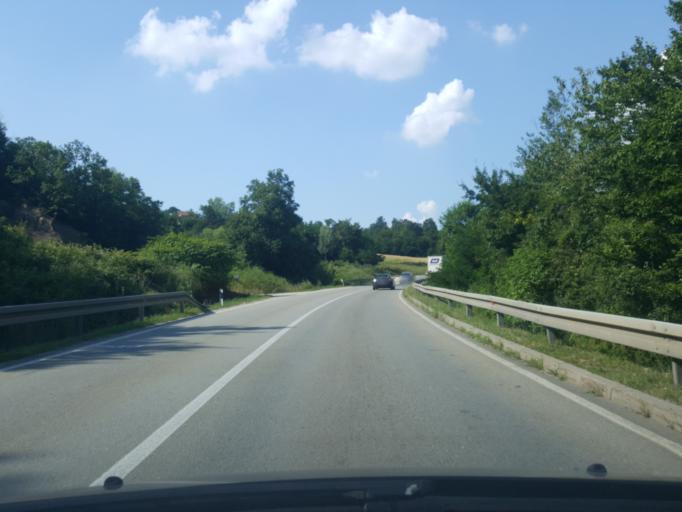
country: RS
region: Central Serbia
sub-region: Moravicki Okrug
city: Gornji Milanovac
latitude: 44.1104
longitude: 20.4832
